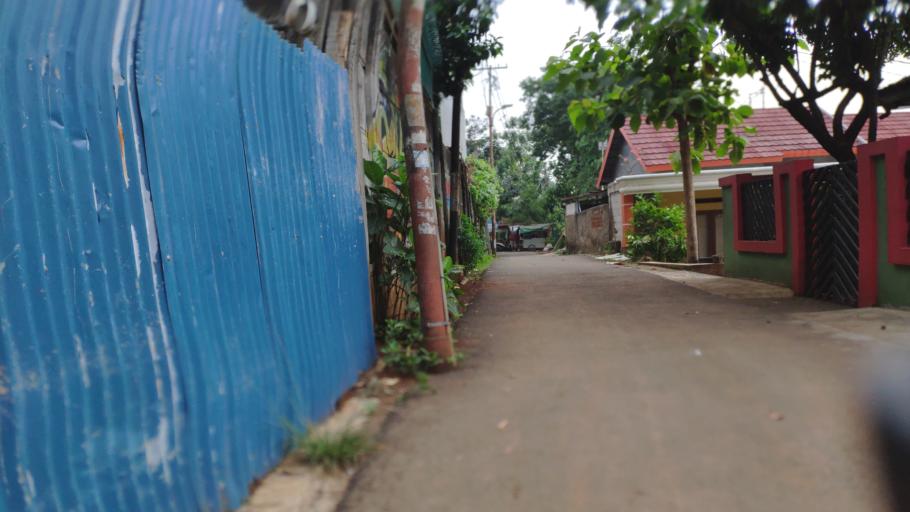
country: ID
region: West Java
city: Depok
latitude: -6.3206
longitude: 106.8232
